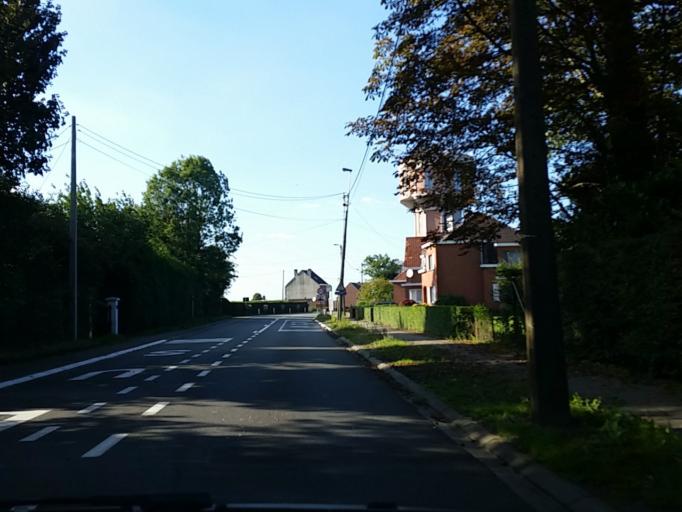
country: BE
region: Flanders
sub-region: Provincie Vlaams-Brabant
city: Kortenberg
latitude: 50.8955
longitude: 4.5340
